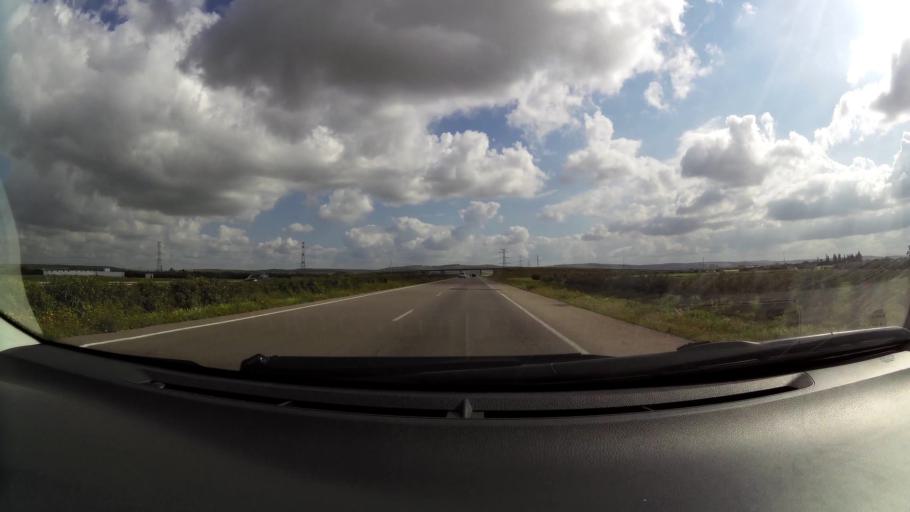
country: MA
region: Chaouia-Ouardigha
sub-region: Settat Province
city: Settat
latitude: 33.1163
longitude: -7.5811
